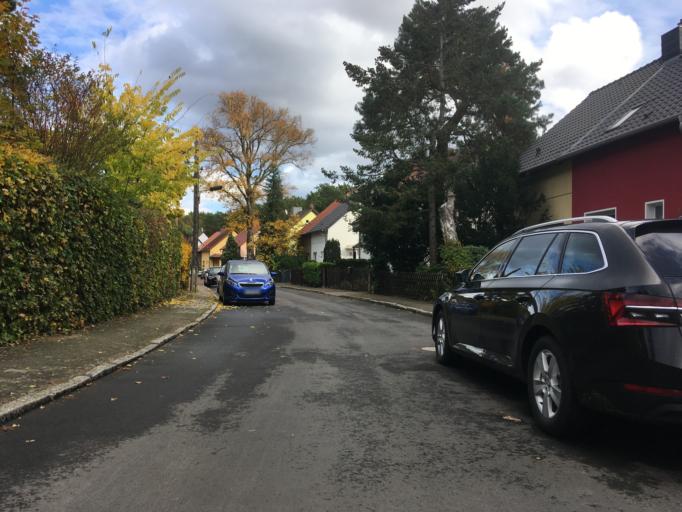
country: DE
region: Berlin
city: Adlershof
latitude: 52.4485
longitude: 13.5398
